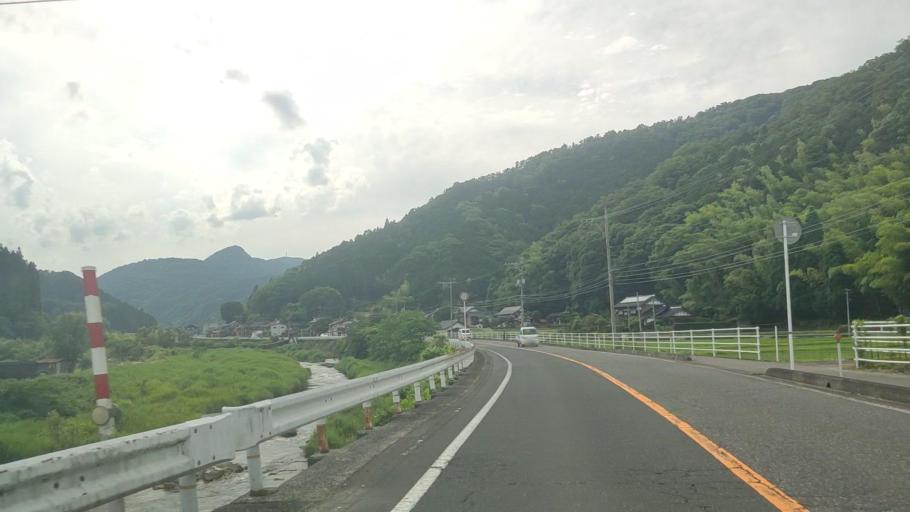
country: JP
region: Tottori
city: Tottori
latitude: 35.3417
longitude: 134.1774
